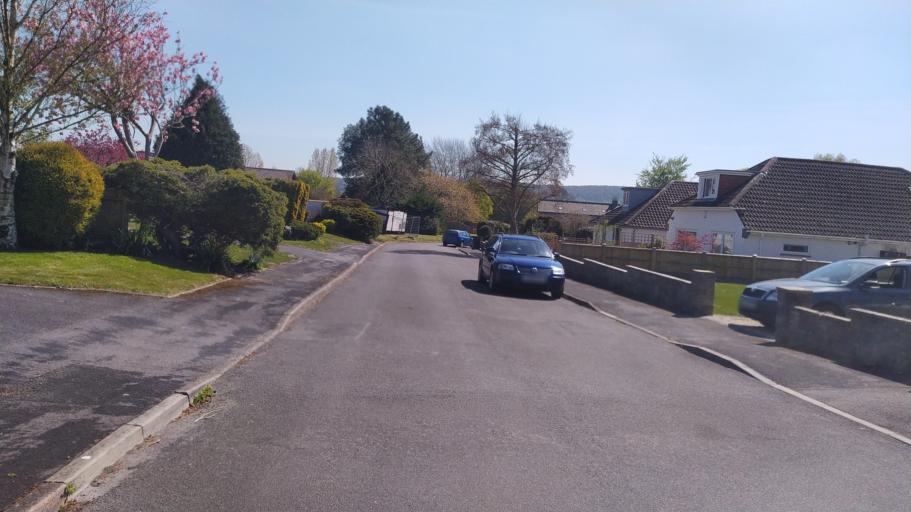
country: GB
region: England
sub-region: Dorset
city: Manston
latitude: 50.9112
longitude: -2.2395
